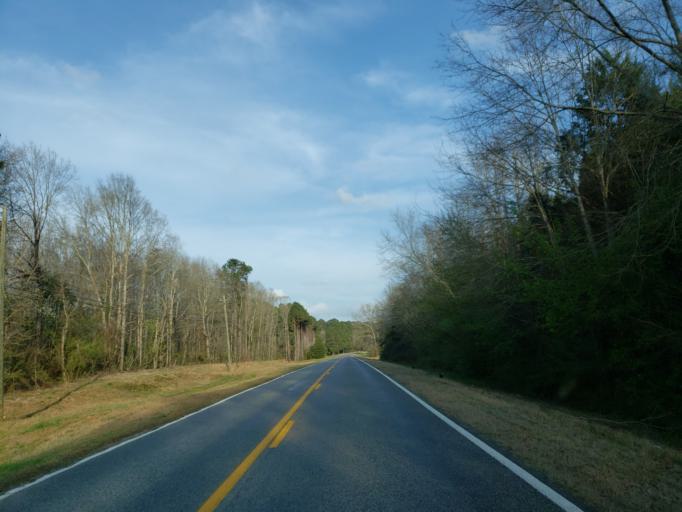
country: US
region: Mississippi
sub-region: Clarke County
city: Stonewall
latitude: 32.1776
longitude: -88.8038
